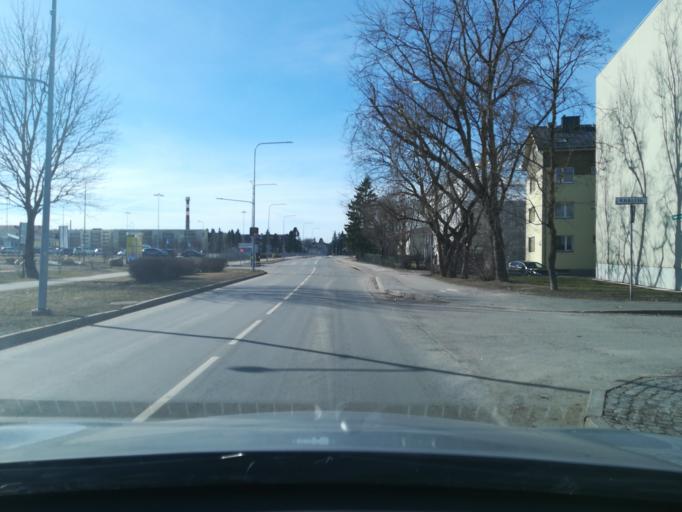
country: EE
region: Harju
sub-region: Saue vald
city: Laagri
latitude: 59.3513
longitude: 24.6212
